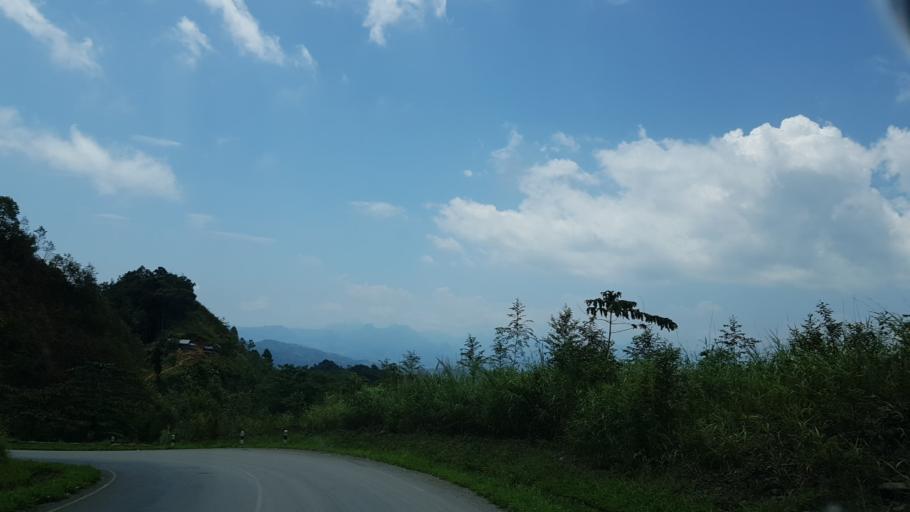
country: LA
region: Vientiane
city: Muang Kasi
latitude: 19.3803
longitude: 102.1552
